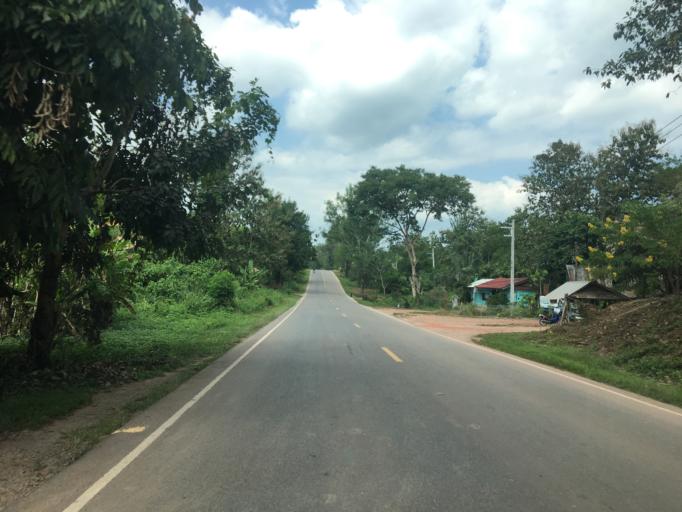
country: TH
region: Nan
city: Nan
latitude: 18.8442
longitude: 100.6553
